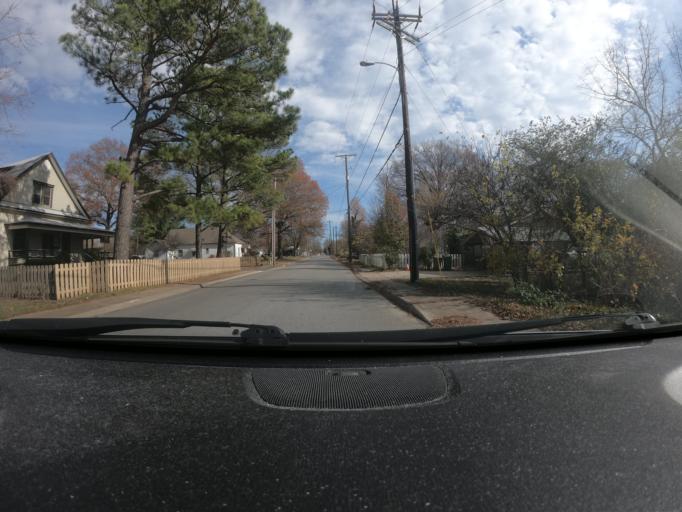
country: US
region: Arkansas
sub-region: Benton County
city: Rogers
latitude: 36.3372
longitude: -94.1241
